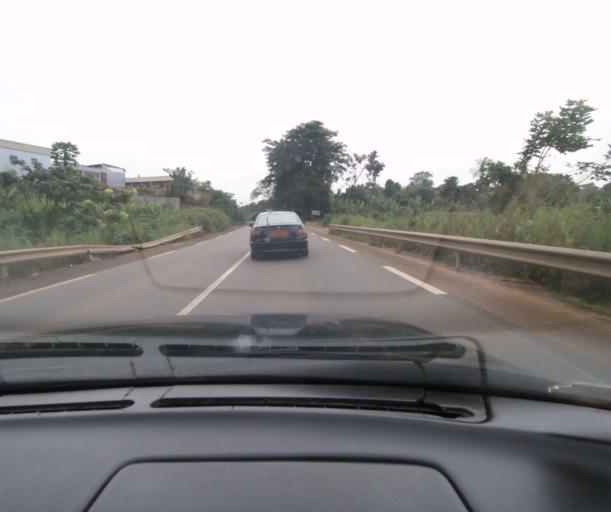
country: CM
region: Centre
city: Obala
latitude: 4.1794
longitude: 11.4722
